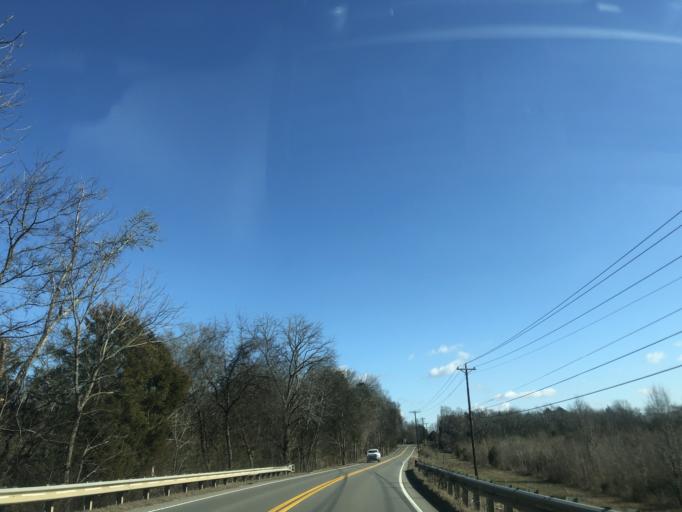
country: US
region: Tennessee
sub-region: Rutherford County
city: Smyrna
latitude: 35.9880
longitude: -86.4250
